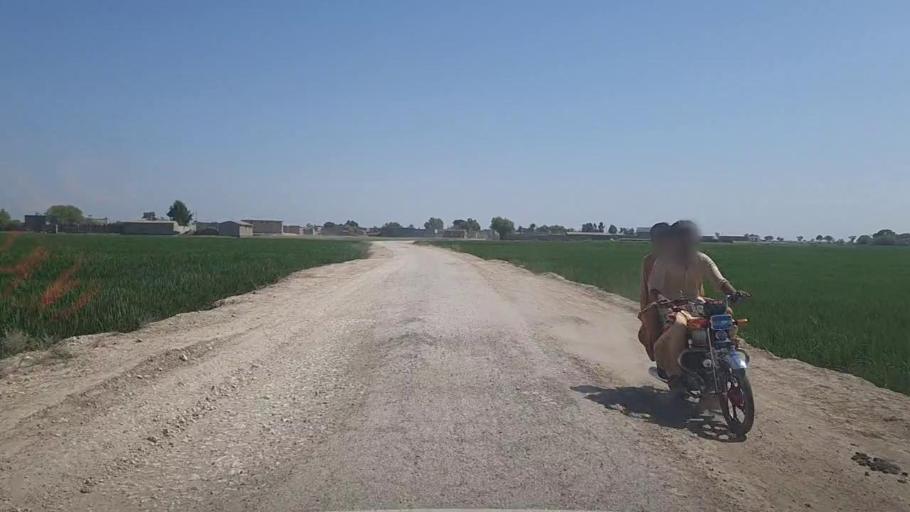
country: PK
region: Sindh
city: Kashmor
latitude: 28.2910
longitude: 69.4348
